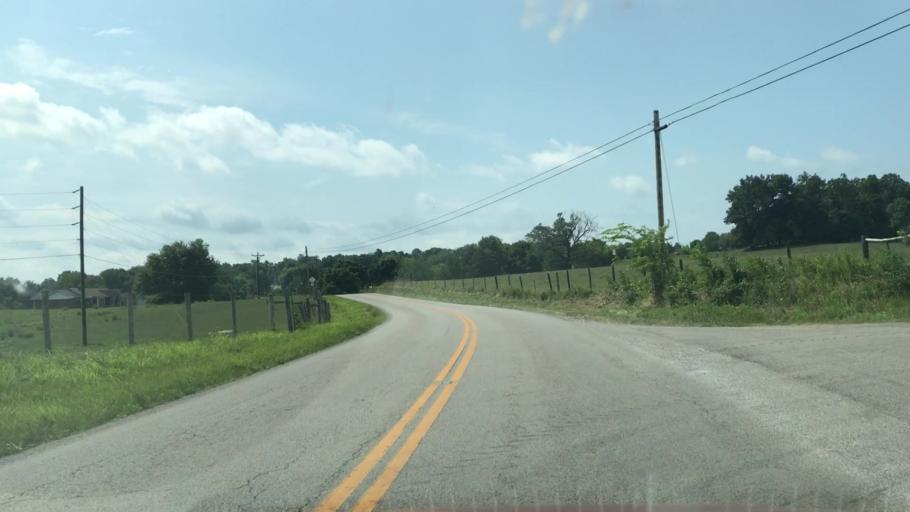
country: US
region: Kentucky
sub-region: Barren County
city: Glasgow
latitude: 36.9062
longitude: -85.8682
